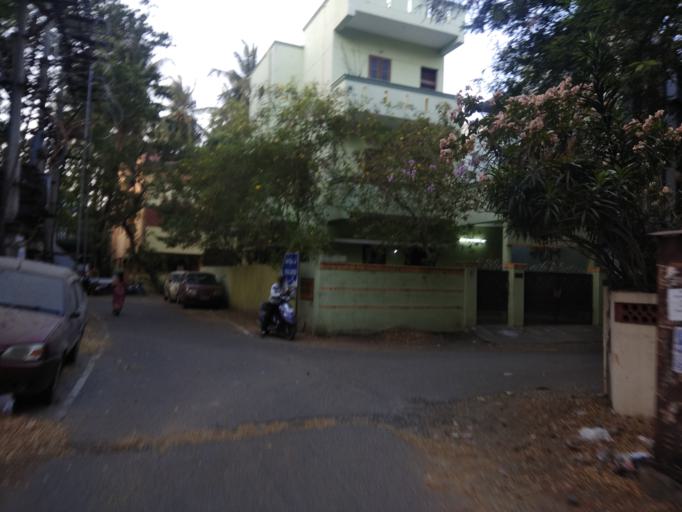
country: IN
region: Tamil Nadu
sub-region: Chennai
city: Chetput
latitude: 13.0718
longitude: 80.2095
